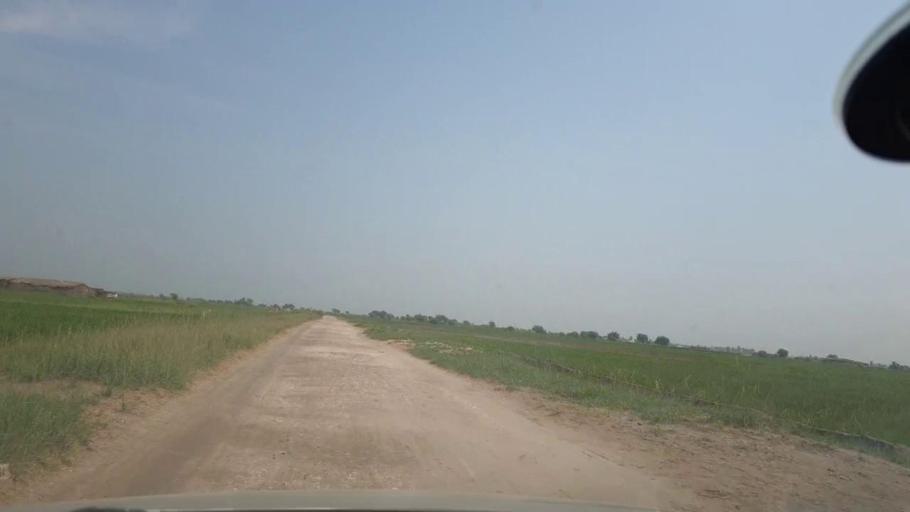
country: PK
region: Sindh
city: Jacobabad
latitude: 28.1401
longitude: 68.3643
